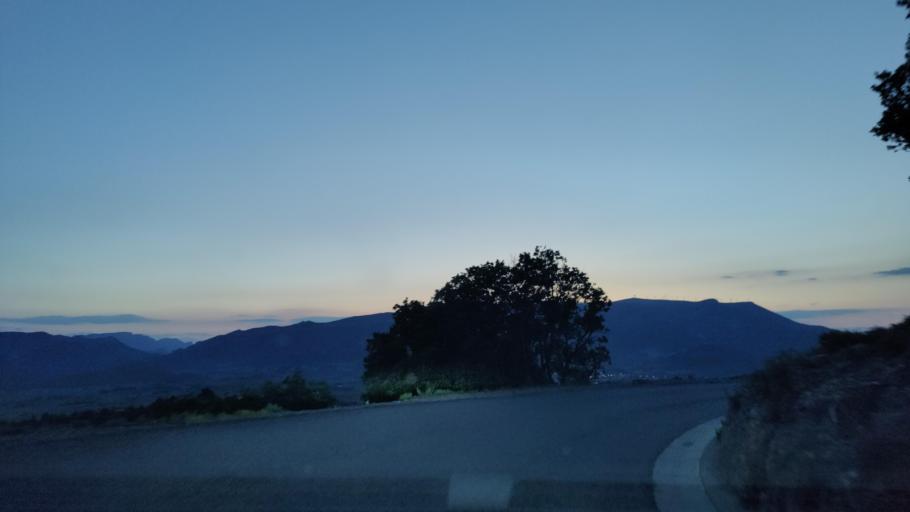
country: FR
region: Languedoc-Roussillon
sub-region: Departement des Pyrenees-Orientales
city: Estagel
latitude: 42.8763
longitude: 2.7539
